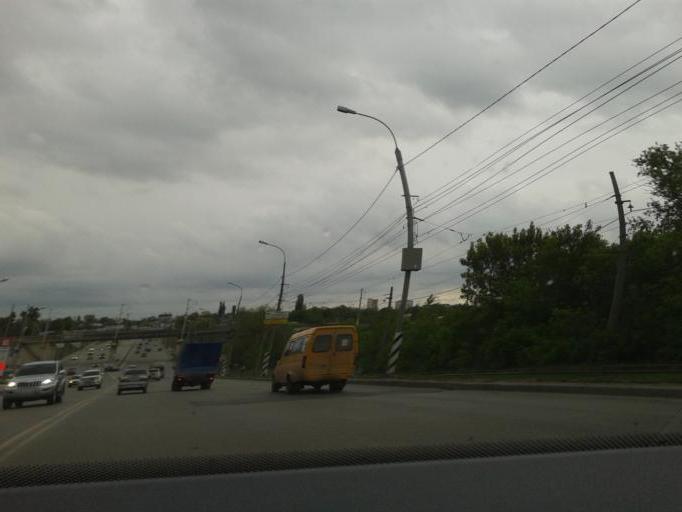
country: RU
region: Volgograd
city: Volgograd
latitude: 48.6855
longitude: 44.4523
